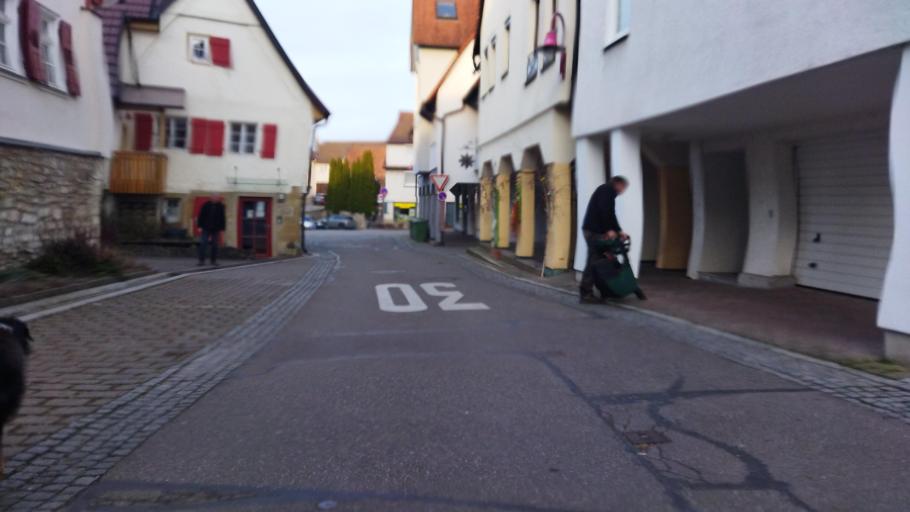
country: DE
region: Baden-Wuerttemberg
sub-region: Regierungsbezirk Stuttgart
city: Freiberg am Neckar
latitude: 48.9401
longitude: 9.1847
